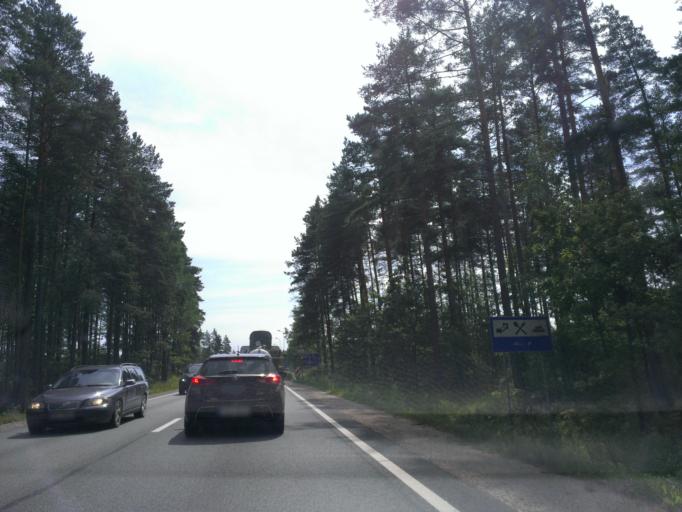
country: LV
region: Salaspils
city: Salaspils
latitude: 56.9457
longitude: 24.3809
